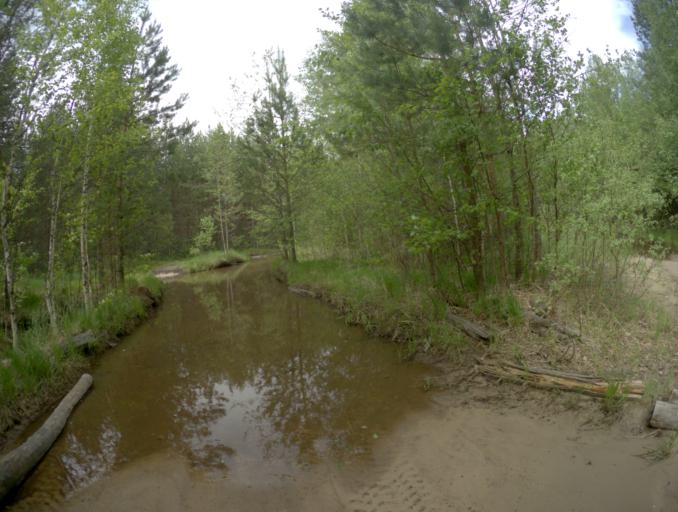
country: RU
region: Vladimir
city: Ivanishchi
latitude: 55.7487
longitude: 40.3777
